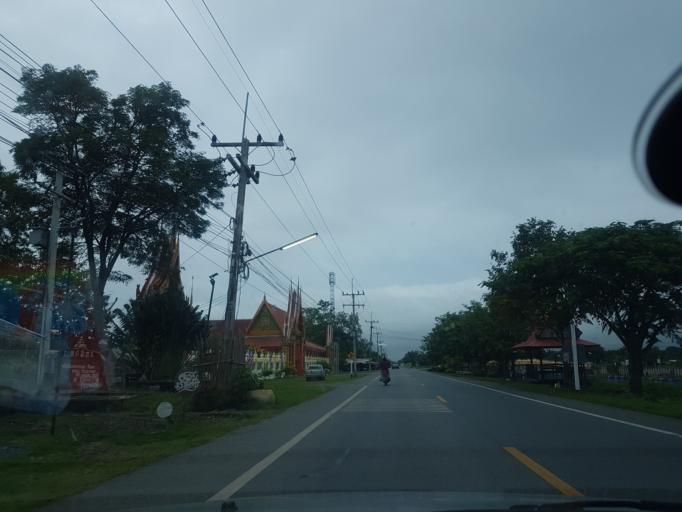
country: TH
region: Pathum Thani
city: Nong Suea
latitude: 14.1788
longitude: 100.8921
